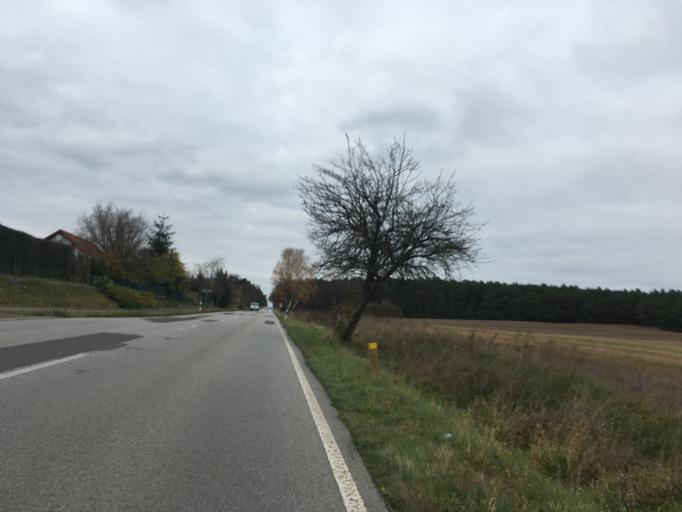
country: DE
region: Brandenburg
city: Mixdorf
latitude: 52.1912
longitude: 14.4639
